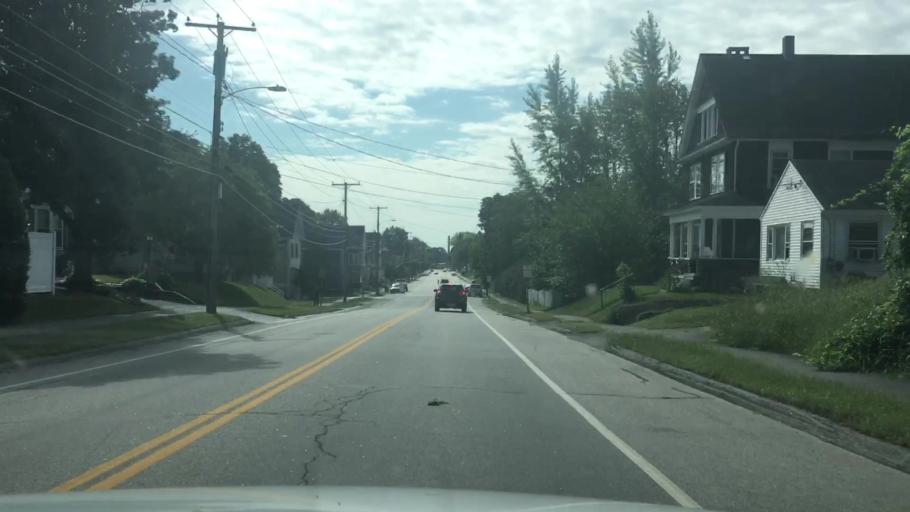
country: US
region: Maine
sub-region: Androscoggin County
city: Auburn
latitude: 44.1073
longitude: -70.2315
